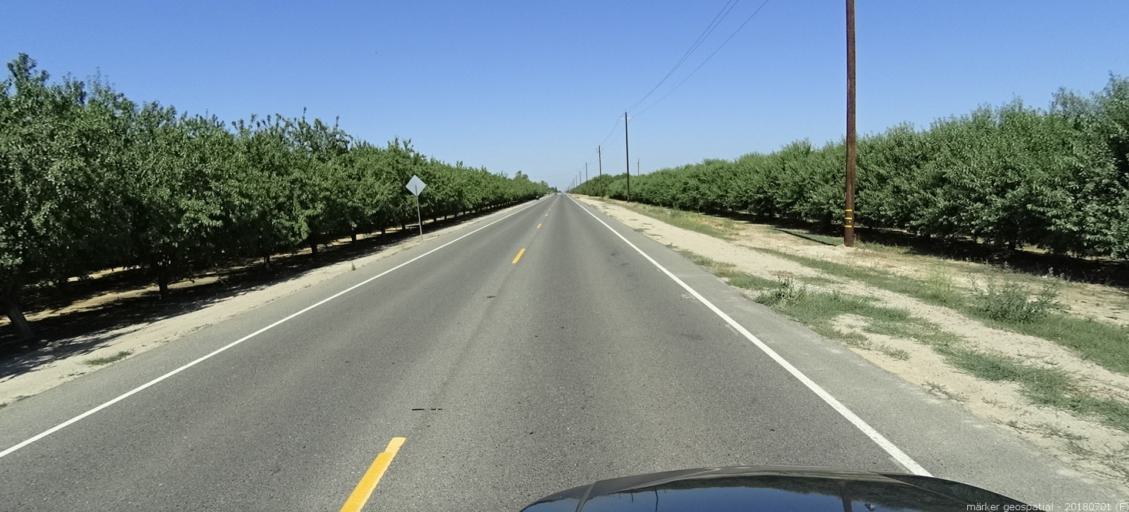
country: US
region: California
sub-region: Madera County
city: Bonadelle Ranchos-Madera Ranchos
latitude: 36.8803
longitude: -119.9138
